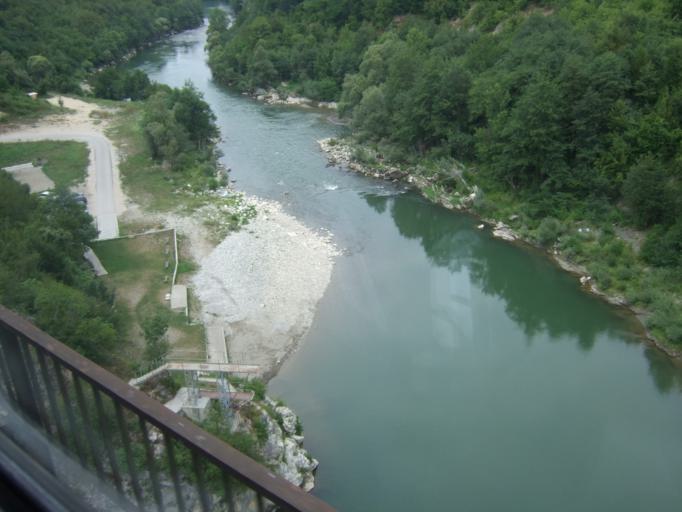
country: RS
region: Central Serbia
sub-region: Zlatiborski Okrug
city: Prijepolje
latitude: 43.3212
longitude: 19.6778
